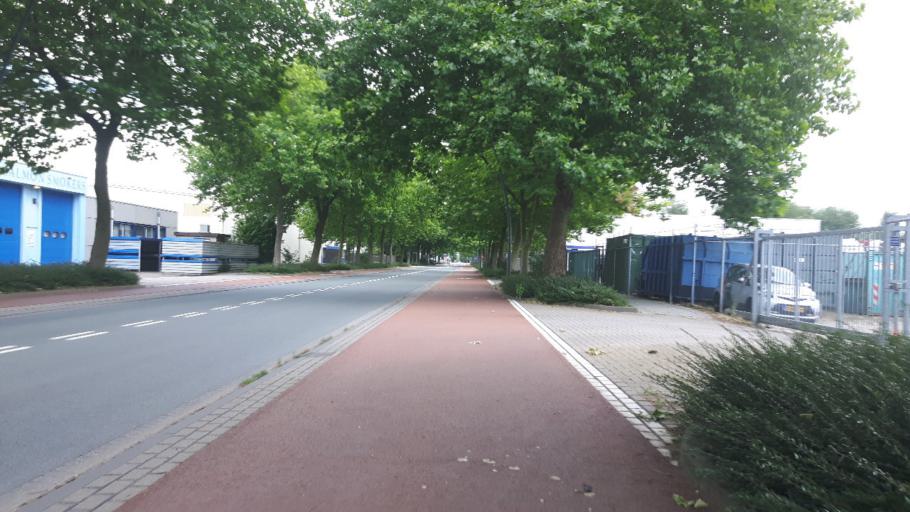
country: NL
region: South Holland
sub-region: Gemeente Capelle aan den IJssel
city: Capelle-West
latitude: 51.9062
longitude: 4.5773
